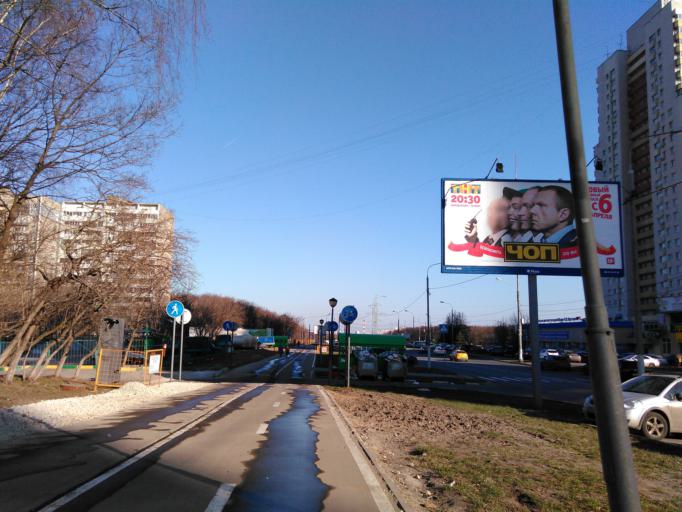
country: RU
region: Moscow
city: Zyuzino
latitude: 55.6390
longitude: 37.5400
